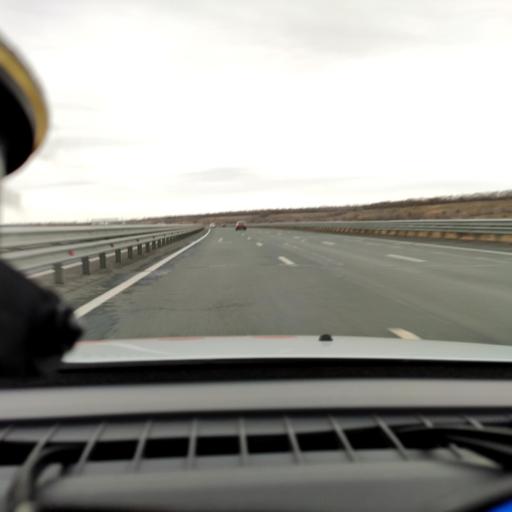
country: RU
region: Samara
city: Smyshlyayevka
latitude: 53.1508
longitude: 50.3579
